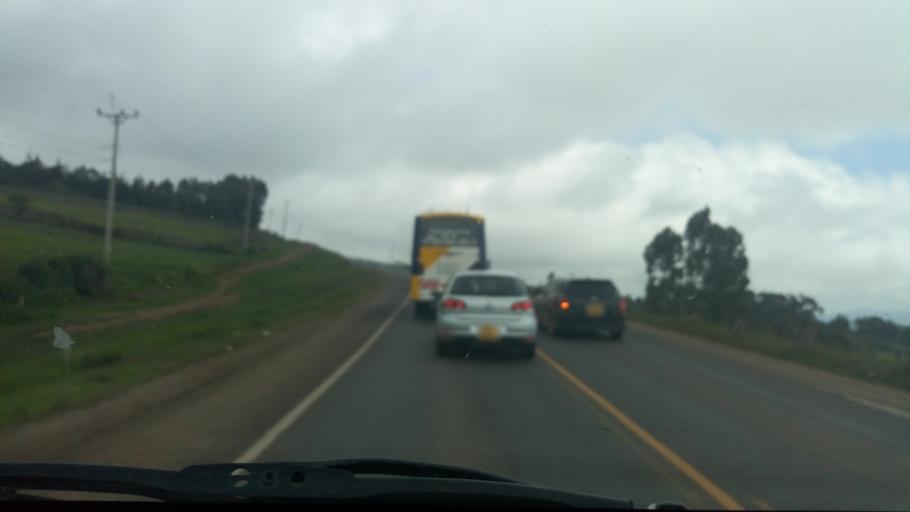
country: KE
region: Nakuru
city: Kijabe
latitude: -0.8463
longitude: 36.5484
